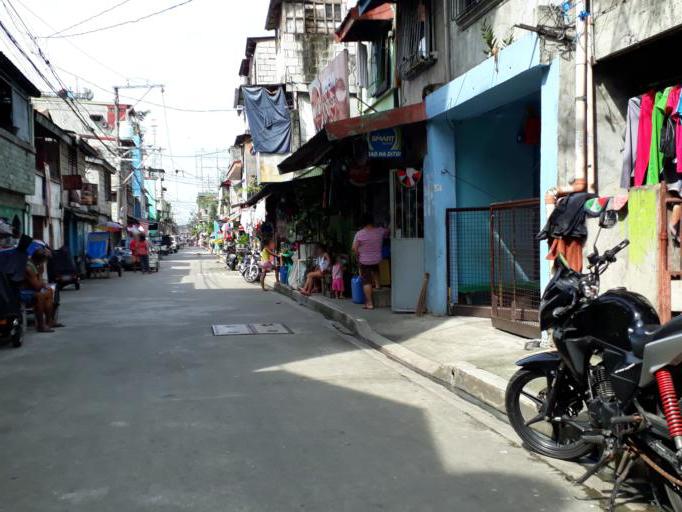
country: PH
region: Calabarzon
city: Del Monte
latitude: 14.6664
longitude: 121.0022
